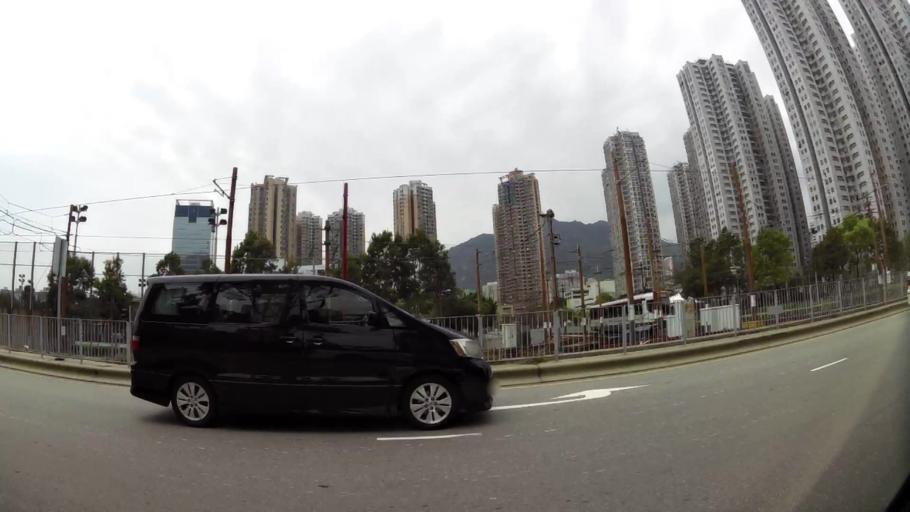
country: HK
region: Tuen Mun
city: Tuen Mun
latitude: 22.3831
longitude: 113.9750
